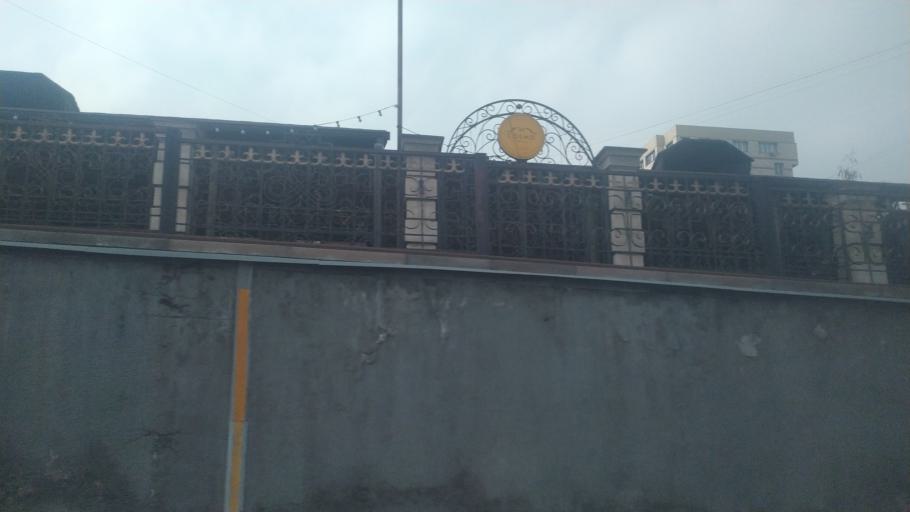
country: KZ
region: Almaty Qalasy
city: Almaty
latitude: 43.1962
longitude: 76.8942
